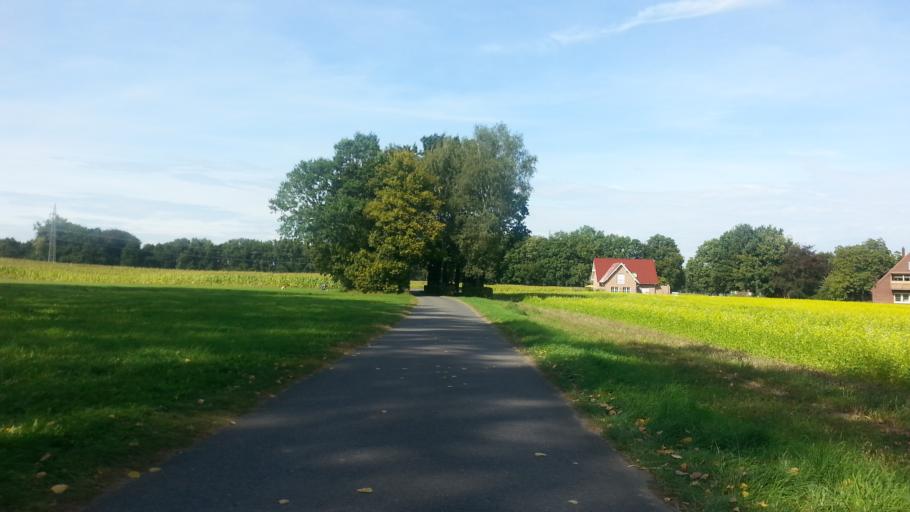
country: DE
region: North Rhine-Westphalia
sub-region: Regierungsbezirk Munster
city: Muenster
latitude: 51.9819
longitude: 7.6002
